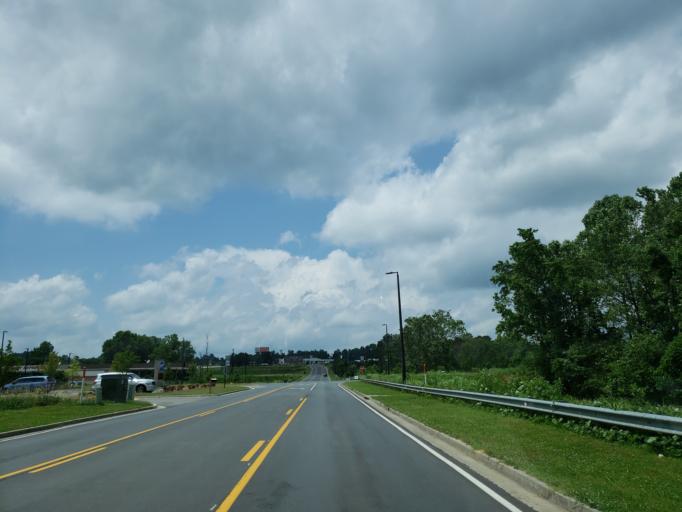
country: US
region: Georgia
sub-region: Pickens County
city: Jasper
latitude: 34.4727
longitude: -84.4611
